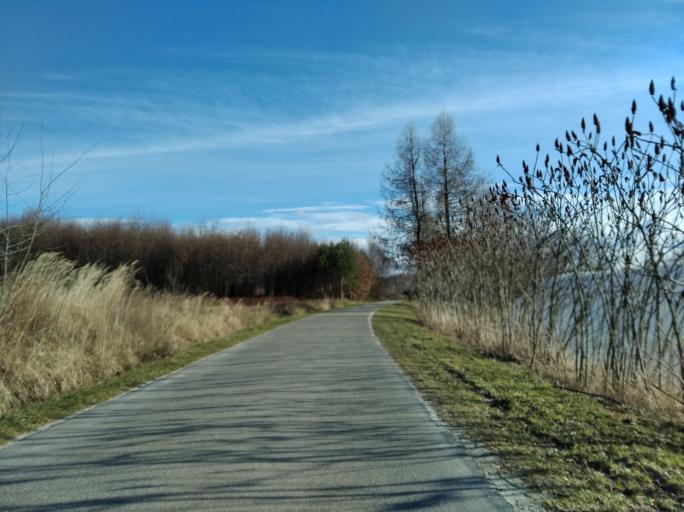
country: PL
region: Subcarpathian Voivodeship
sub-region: Powiat strzyzowski
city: Wisniowa
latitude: 49.9006
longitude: 21.6630
